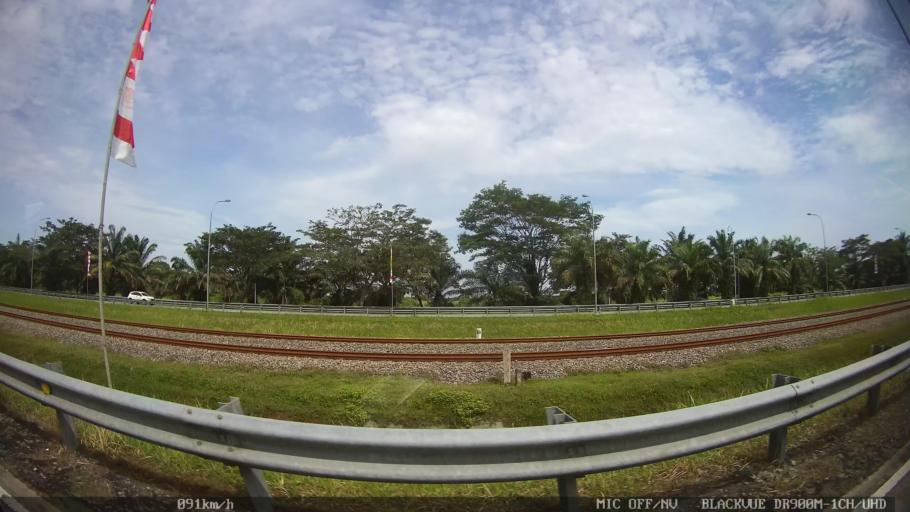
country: ID
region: North Sumatra
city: Percut
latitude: 3.6222
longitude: 98.8660
